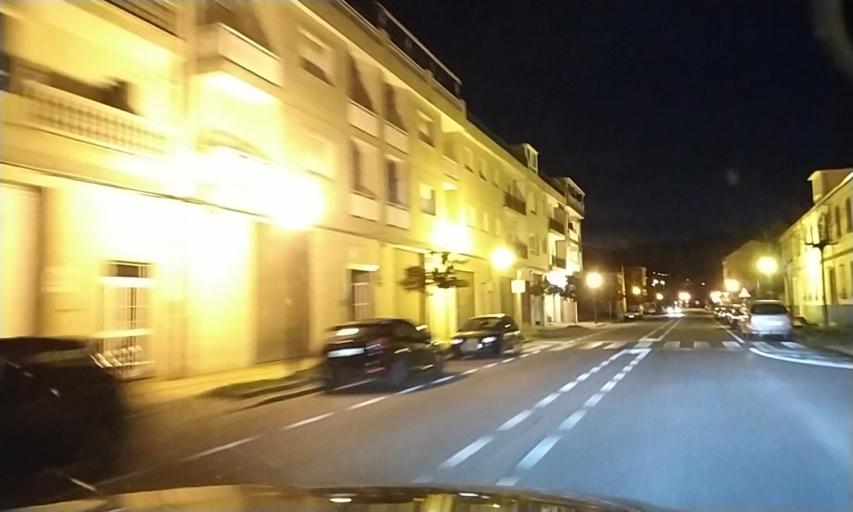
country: ES
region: Galicia
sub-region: Provincia de Ourense
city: Verin
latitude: 41.9400
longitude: -7.4256
